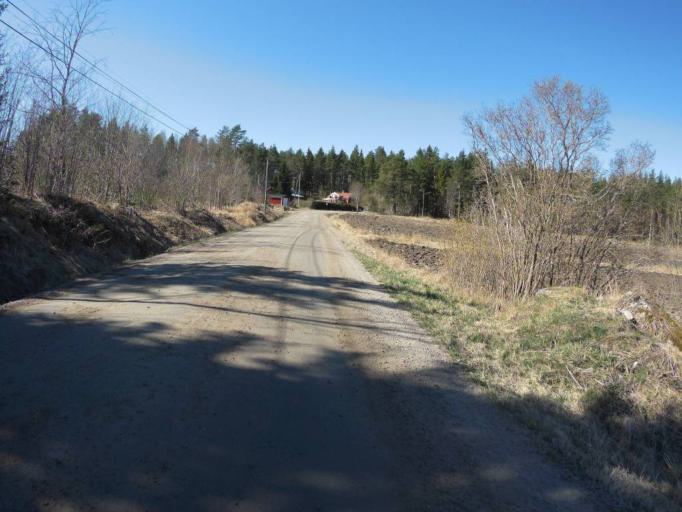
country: SE
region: Gaevleborg
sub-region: Gavle Kommun
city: Gavle
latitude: 60.7305
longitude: 17.2016
